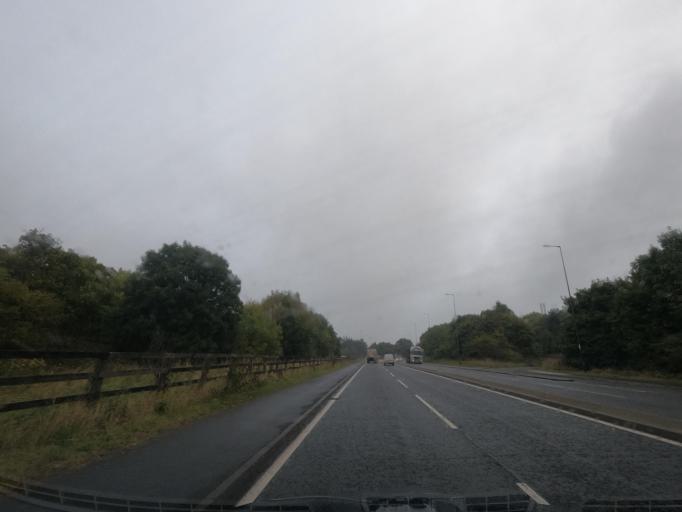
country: GB
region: England
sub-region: Redcar and Cleveland
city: South Bank
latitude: 54.5861
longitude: -1.1340
